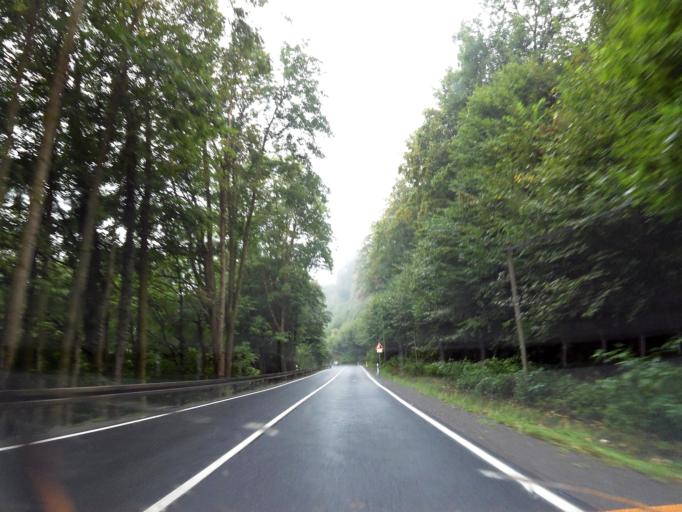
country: DE
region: Thuringia
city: Ilfeld
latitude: 51.6014
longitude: 10.7858
